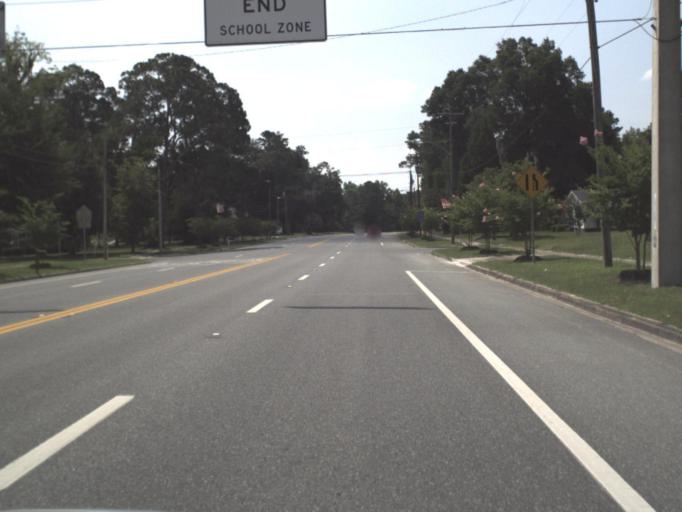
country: US
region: Georgia
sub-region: Echols County
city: Statenville
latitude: 30.6018
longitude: -83.0988
